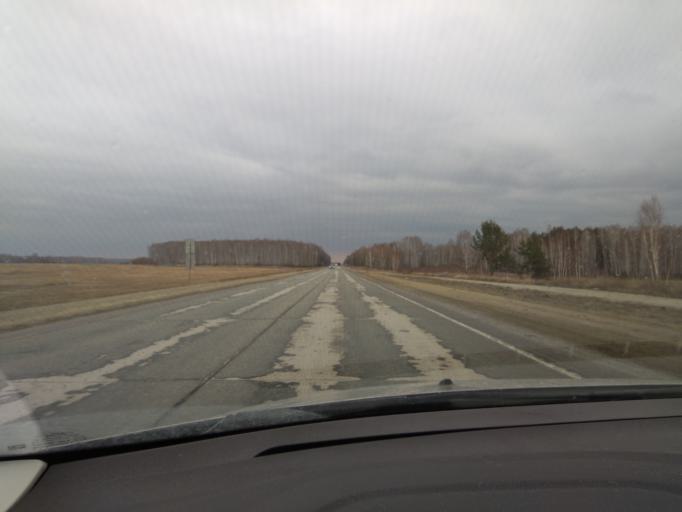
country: RU
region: Chelyabinsk
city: Tyubuk
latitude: 55.9796
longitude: 61.0326
